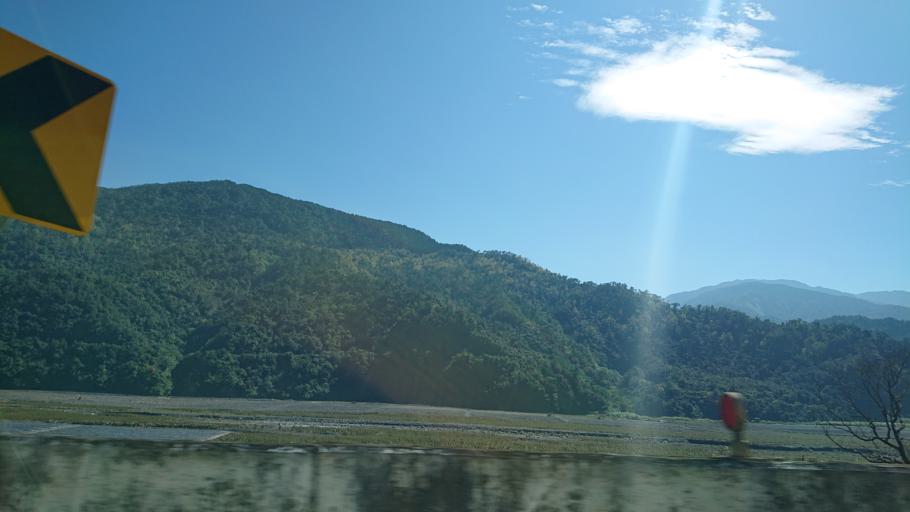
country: TW
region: Taiwan
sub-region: Yilan
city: Yilan
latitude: 24.5866
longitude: 121.5023
